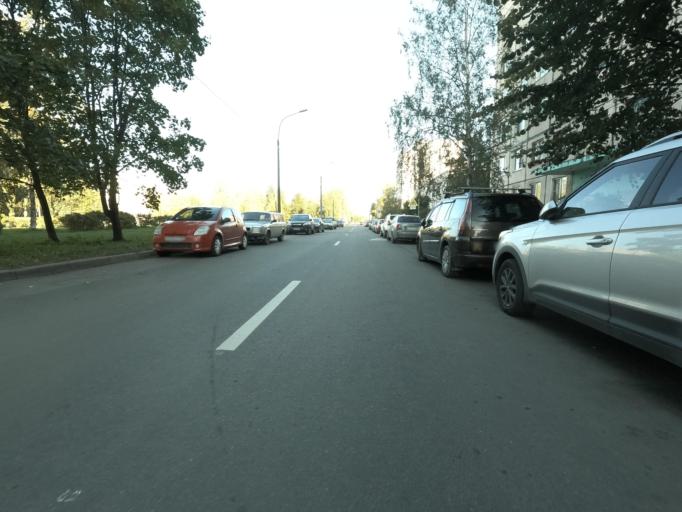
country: RU
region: St.-Petersburg
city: Kolpino
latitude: 59.7378
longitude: 30.5636
